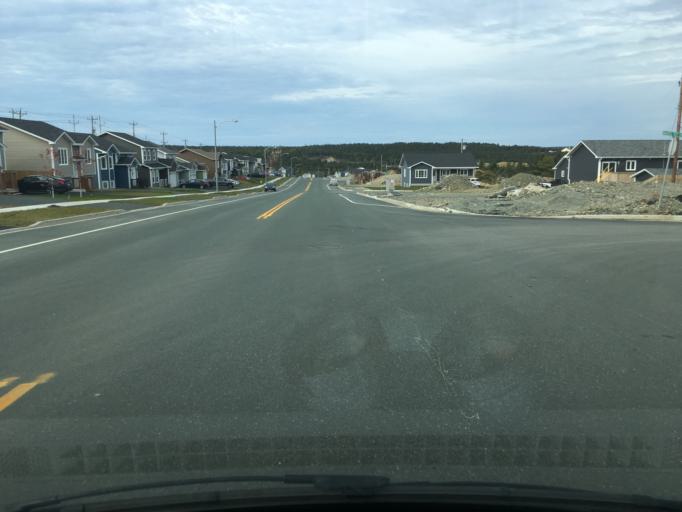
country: CA
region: Newfoundland and Labrador
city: Mount Pearl
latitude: 47.5514
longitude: -52.7896
